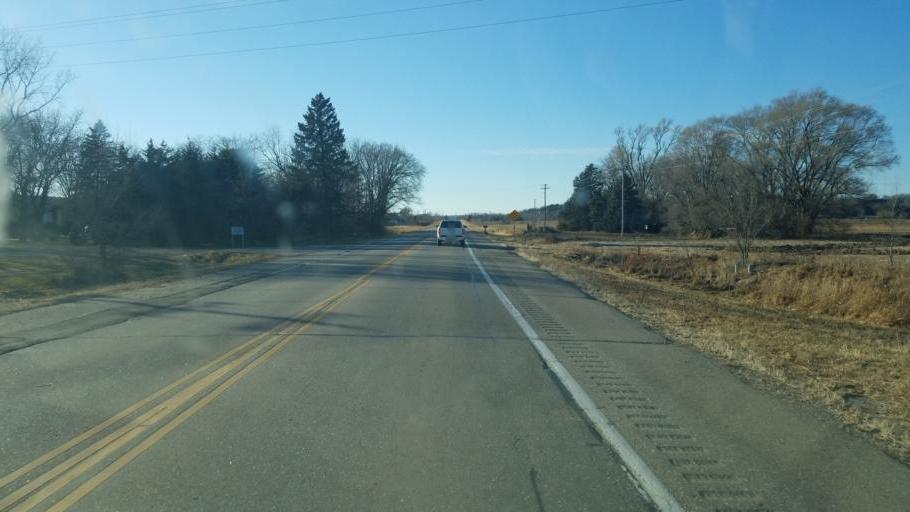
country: US
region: South Dakota
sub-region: Union County
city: Dakota Dunes
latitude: 42.4484
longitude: -96.5488
